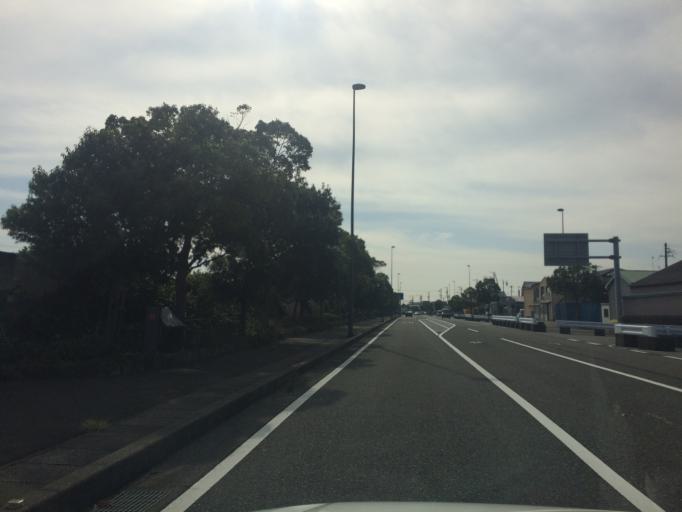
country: JP
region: Shizuoka
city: Yaizu
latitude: 34.8651
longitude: 138.3255
